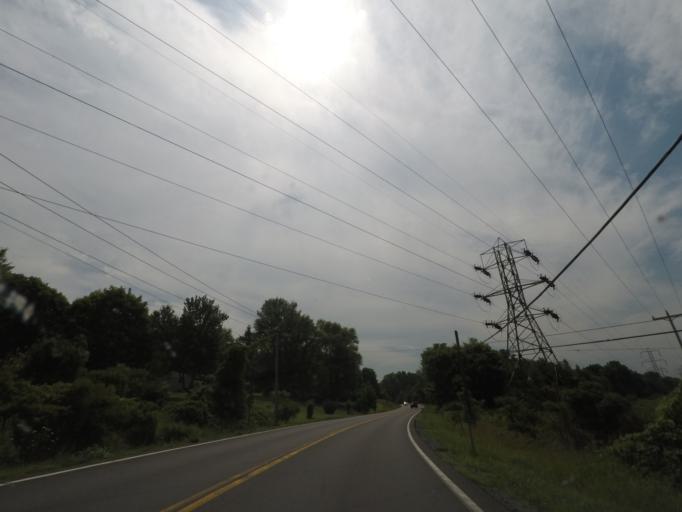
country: US
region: New York
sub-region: Saratoga County
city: Waterford
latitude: 42.7661
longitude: -73.6270
